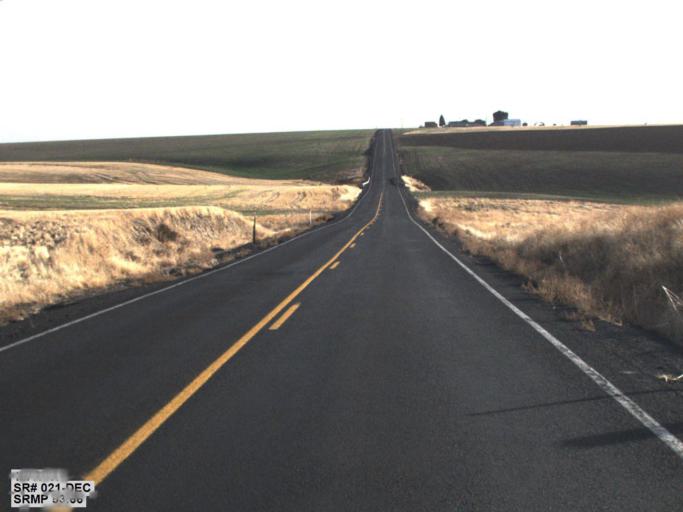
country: US
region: Washington
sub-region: Adams County
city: Ritzville
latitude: 47.3061
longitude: -118.6903
